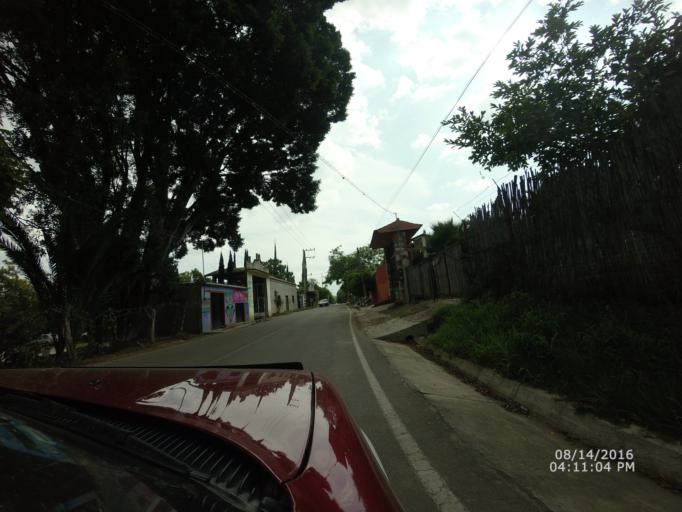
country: MX
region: Oaxaca
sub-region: San Lorenzo Cacaotepec
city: Santiago Etla
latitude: 17.1815
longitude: -96.7651
